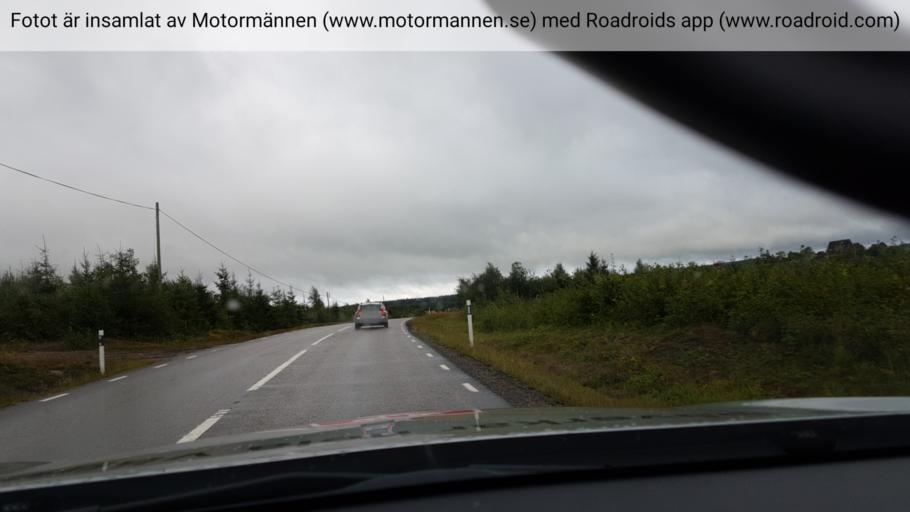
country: SE
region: Vaestra Goetaland
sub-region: Essunga Kommun
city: Nossebro
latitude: 58.1050
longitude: 12.6520
